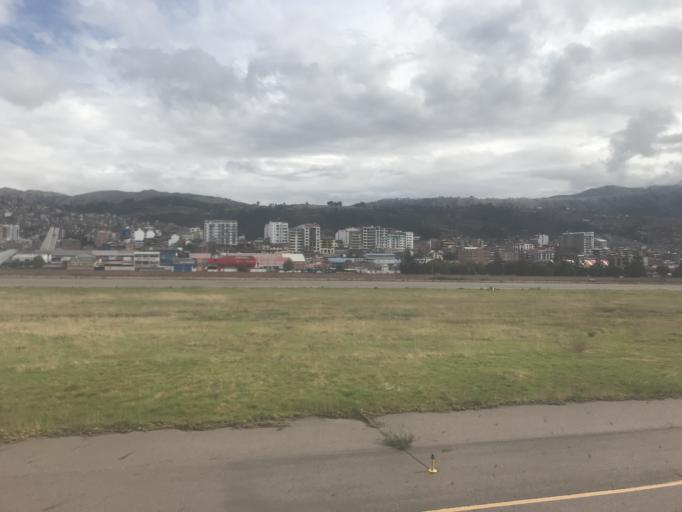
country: PE
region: Cusco
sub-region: Provincia de Cusco
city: Cusco
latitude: -13.5359
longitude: -71.9508
